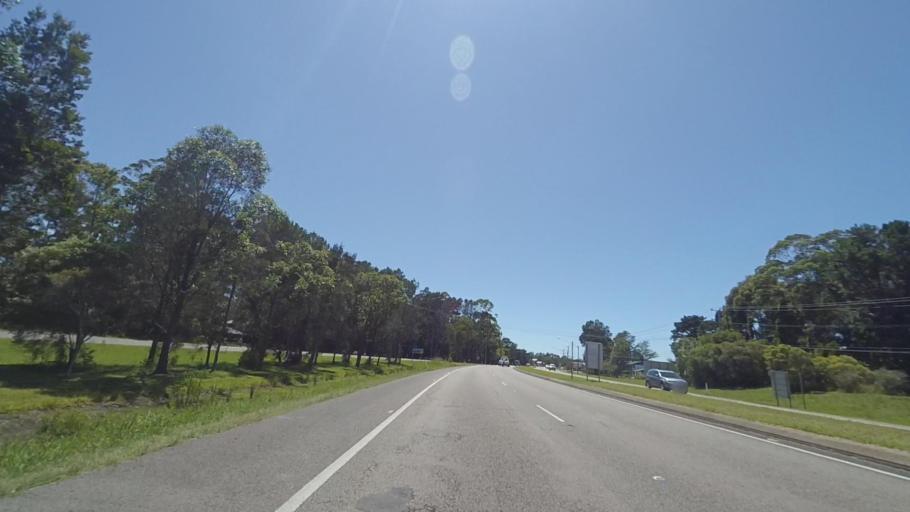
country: AU
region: New South Wales
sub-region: Port Stephens Shire
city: Medowie
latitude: -32.7888
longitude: 151.9048
